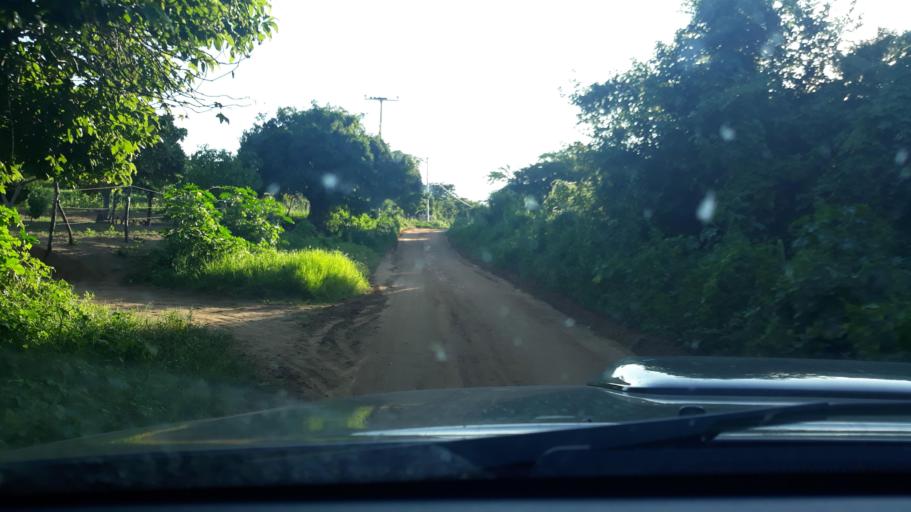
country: BR
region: Bahia
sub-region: Riacho De Santana
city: Riacho de Santana
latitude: -13.8393
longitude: -42.7344
